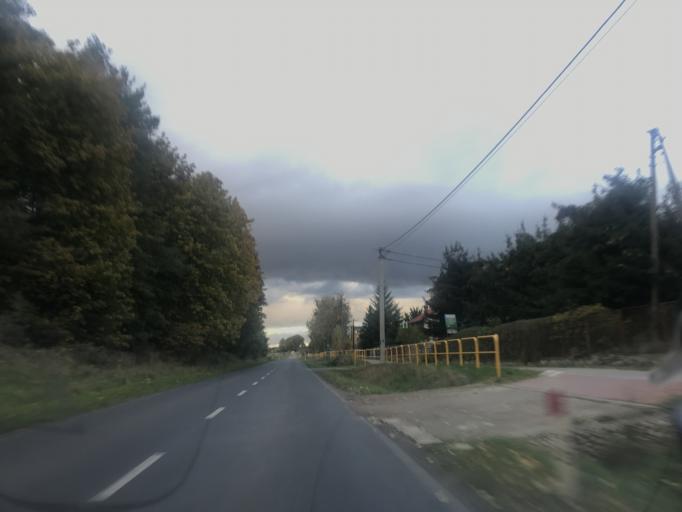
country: PL
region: West Pomeranian Voivodeship
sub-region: Powiat walecki
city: Tuczno
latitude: 53.2084
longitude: 16.1674
